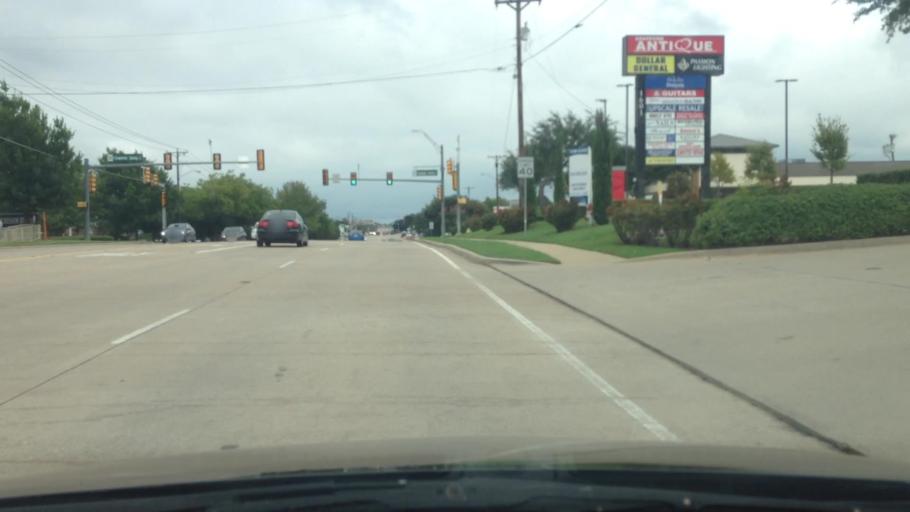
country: US
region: Texas
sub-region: Tarrant County
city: Grapevine
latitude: 32.9410
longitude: -97.0941
